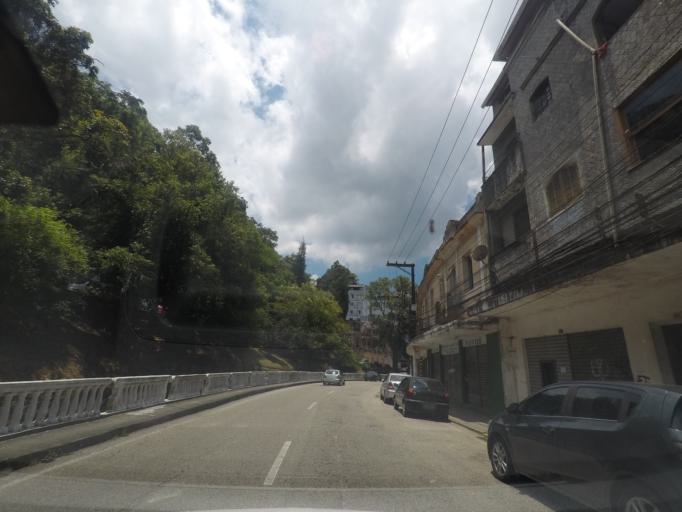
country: BR
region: Rio de Janeiro
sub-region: Petropolis
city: Petropolis
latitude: -22.5132
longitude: -43.1806
